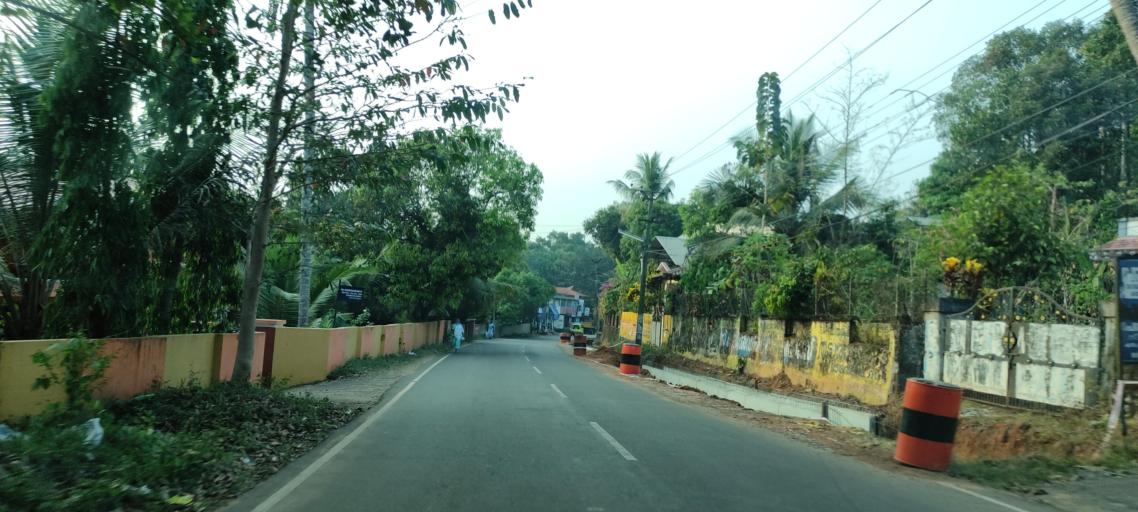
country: IN
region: Kerala
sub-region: Alappuzha
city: Mavelikara
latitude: 9.2513
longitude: 76.5688
